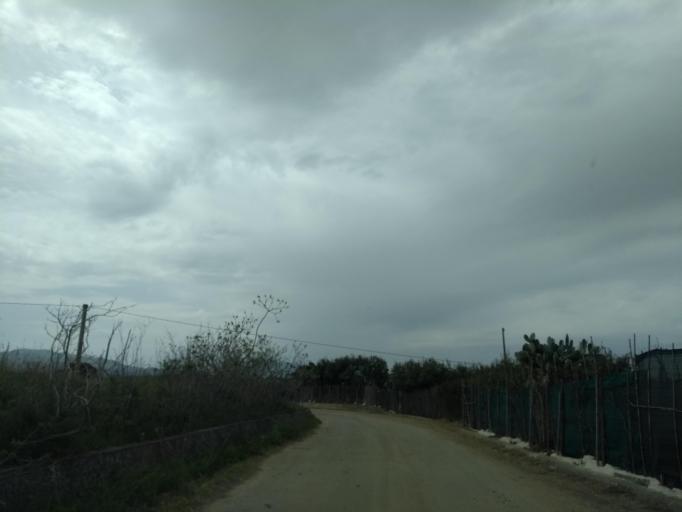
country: IT
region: Sicily
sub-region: Palermo
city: Partinico
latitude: 37.9945
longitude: 13.0776
